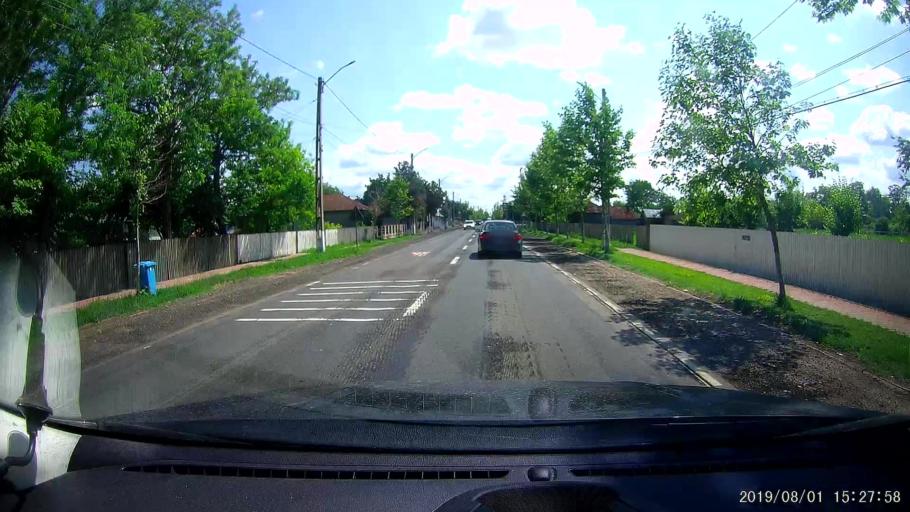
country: RO
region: Braila
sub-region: Comuna Viziru
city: Viziru
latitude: 44.9973
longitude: 27.7126
